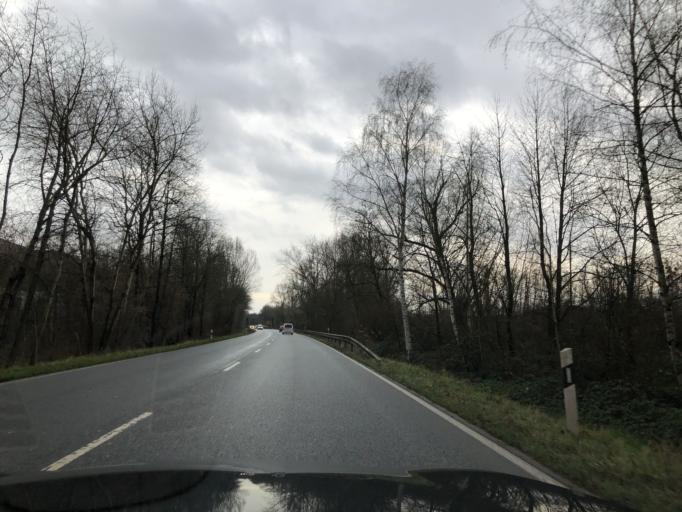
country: DE
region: Rheinland-Pfalz
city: Rheinbreitbach
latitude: 50.6223
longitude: 7.2187
